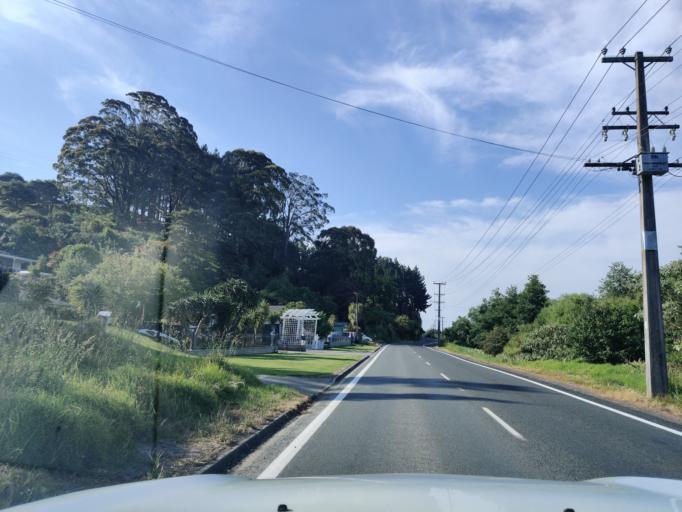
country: NZ
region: Waikato
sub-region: Waikato District
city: Ngaruawahia
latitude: -37.5803
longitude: 175.1537
